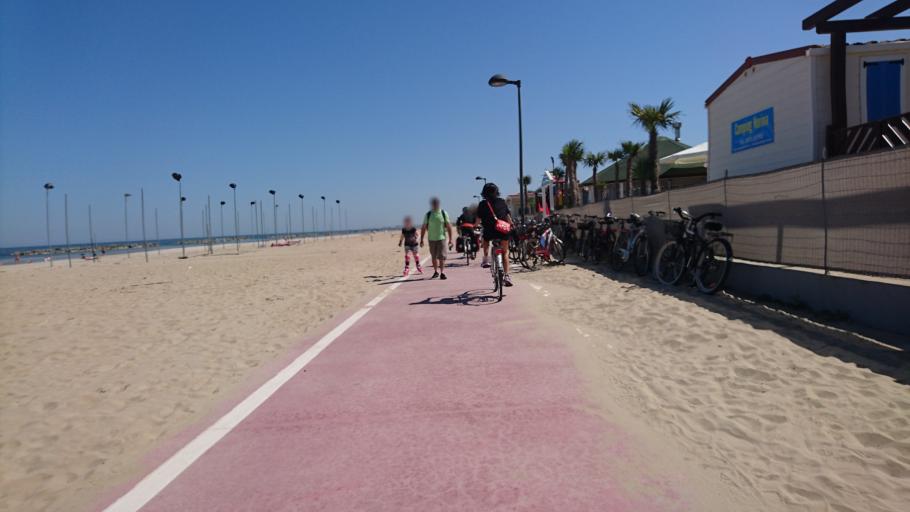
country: IT
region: The Marches
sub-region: Provincia di Pesaro e Urbino
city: Fenile
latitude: 43.8842
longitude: 12.9587
